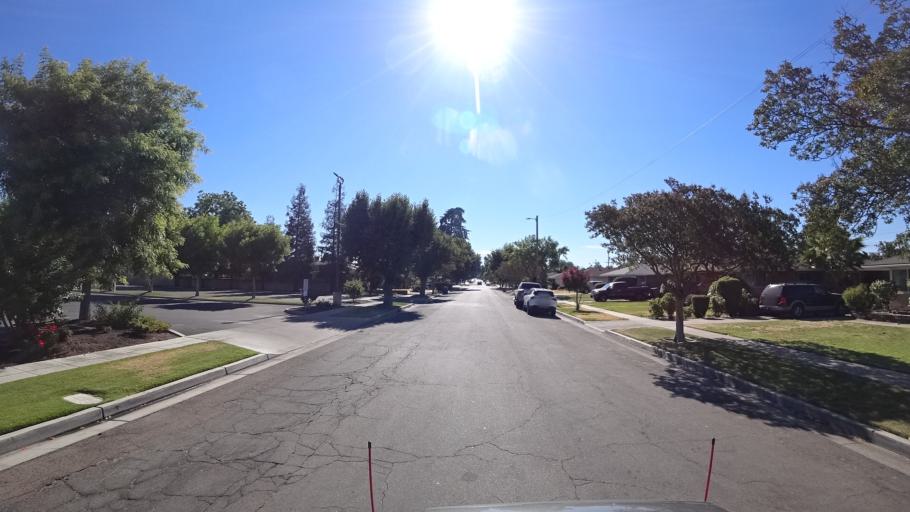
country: US
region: California
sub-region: Fresno County
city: Fresno
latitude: 36.7757
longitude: -119.8258
